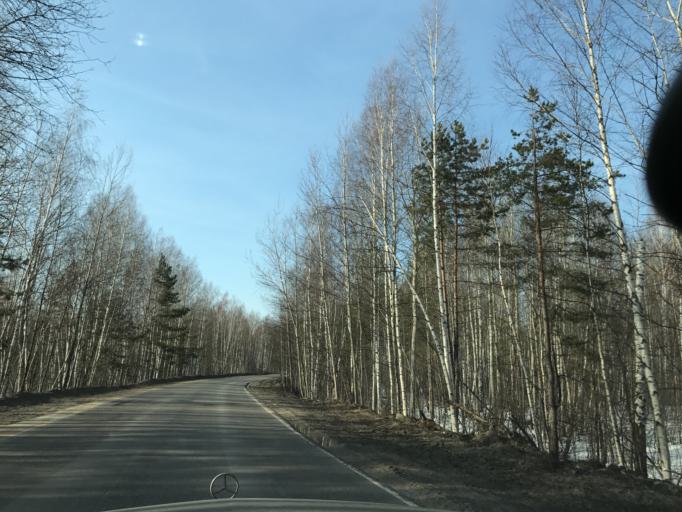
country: RU
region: Vladimir
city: Galitsy
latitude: 56.0010
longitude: 42.8628
